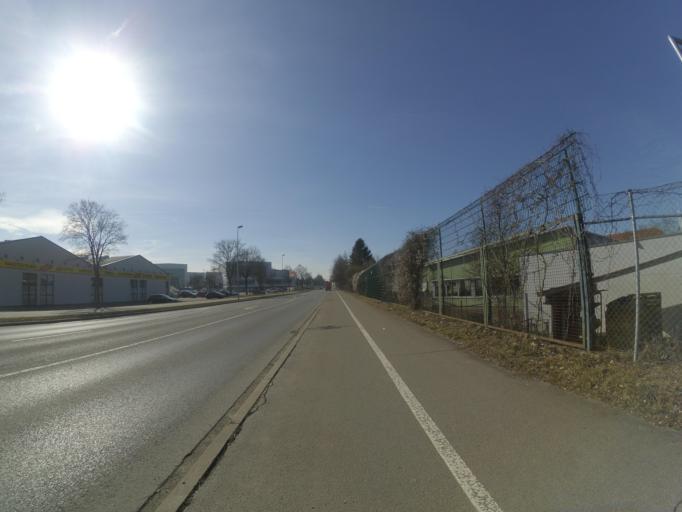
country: DE
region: Baden-Wuerttemberg
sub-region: Tuebingen Region
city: Weingarten
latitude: 47.8169
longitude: 9.6409
